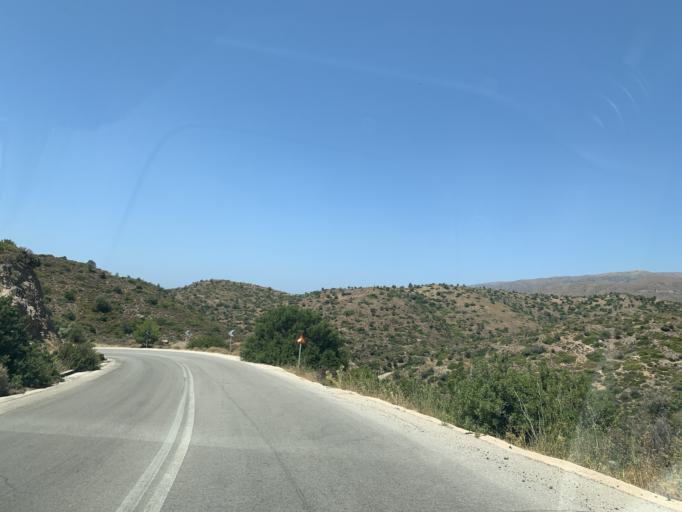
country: GR
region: North Aegean
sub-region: Chios
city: Vrontados
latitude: 38.4692
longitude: 25.9616
